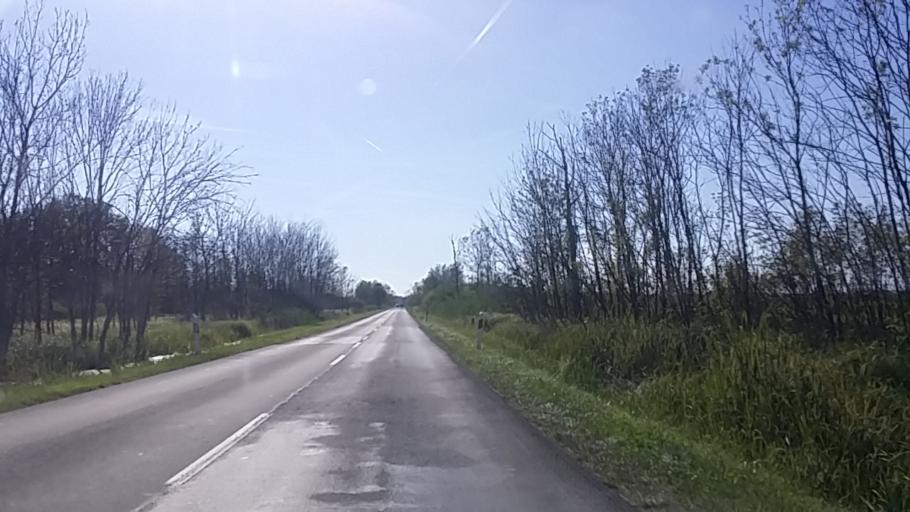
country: HU
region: Zala
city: Sarmellek
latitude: 46.7075
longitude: 17.2072
